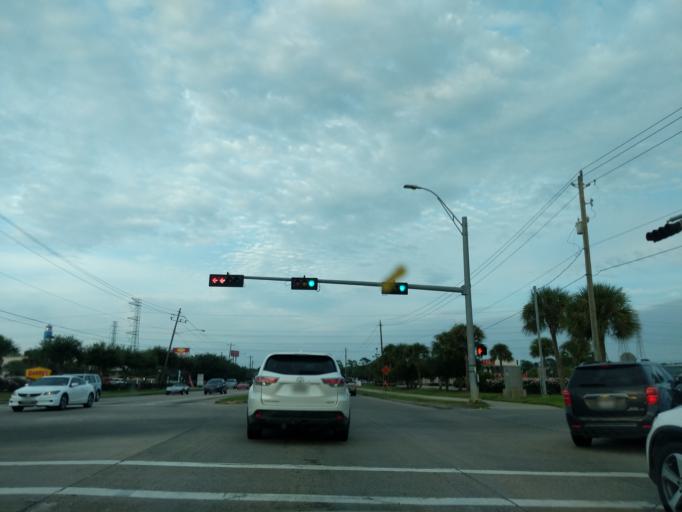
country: US
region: Texas
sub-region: Galveston County
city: Kemah
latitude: 29.5346
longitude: -95.0231
